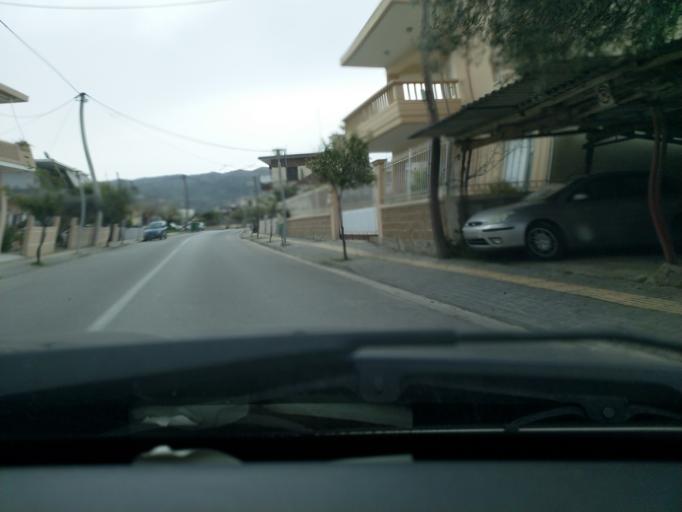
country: GR
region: Crete
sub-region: Nomos Chanias
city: Mournies
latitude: 35.4953
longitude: 24.0225
